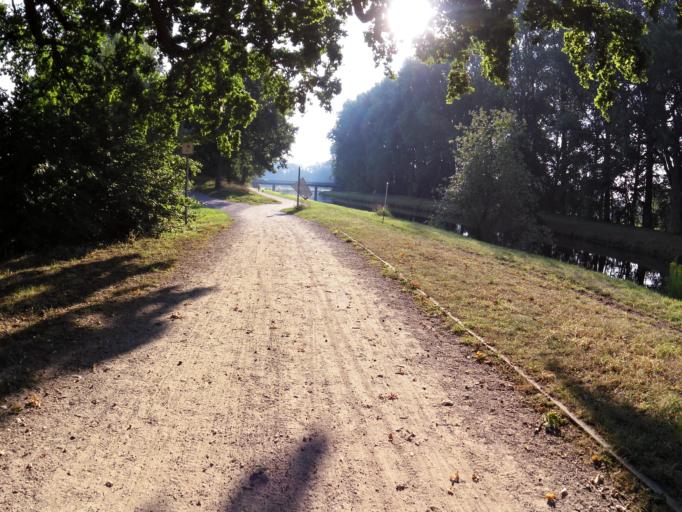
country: DE
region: North Rhine-Westphalia
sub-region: Regierungsbezirk Munster
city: Warendorf
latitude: 51.9551
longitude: 8.0103
